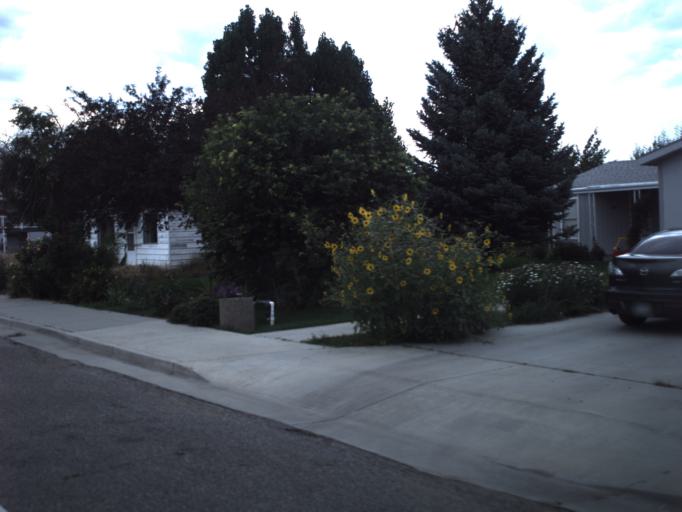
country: US
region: Utah
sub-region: Emery County
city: Huntington
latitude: 39.3487
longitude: -110.8549
